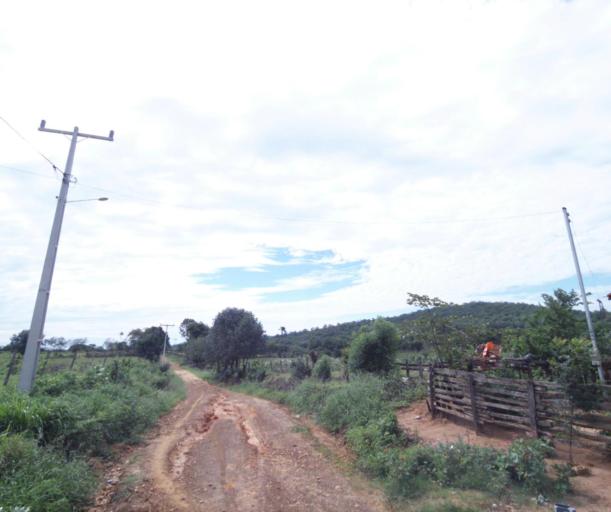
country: BR
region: Bahia
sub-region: Carinhanha
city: Carinhanha
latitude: -14.2383
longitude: -44.3995
